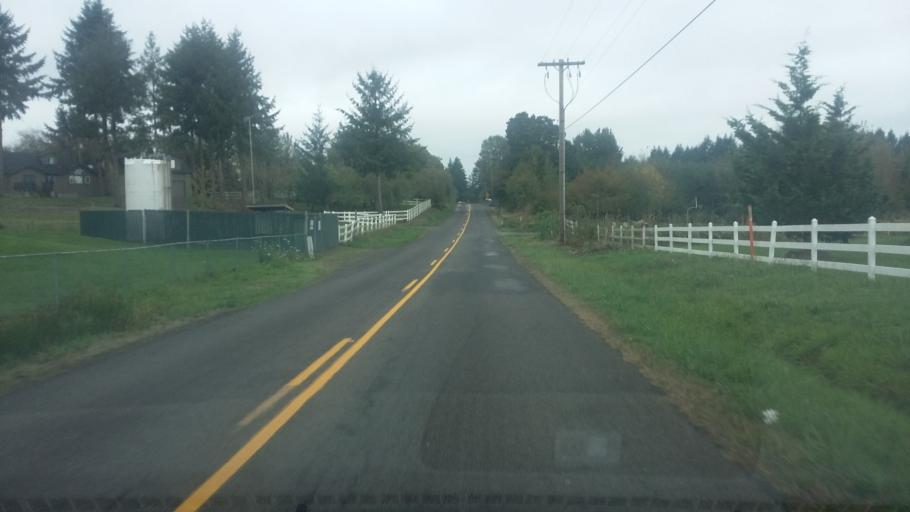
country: US
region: Washington
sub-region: Clark County
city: La Center
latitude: 45.8374
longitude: -122.6905
